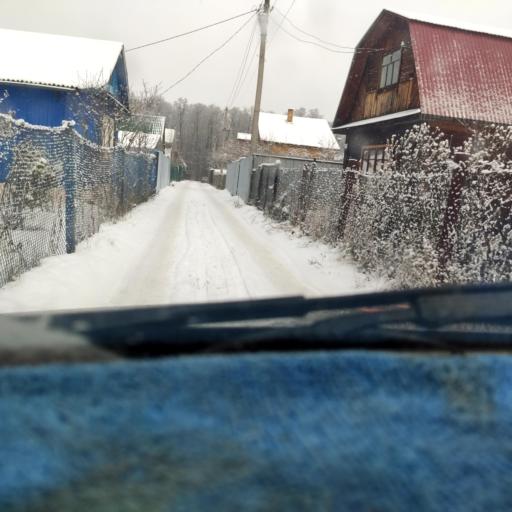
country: RU
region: Bashkortostan
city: Ufa
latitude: 54.6744
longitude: 55.8531
